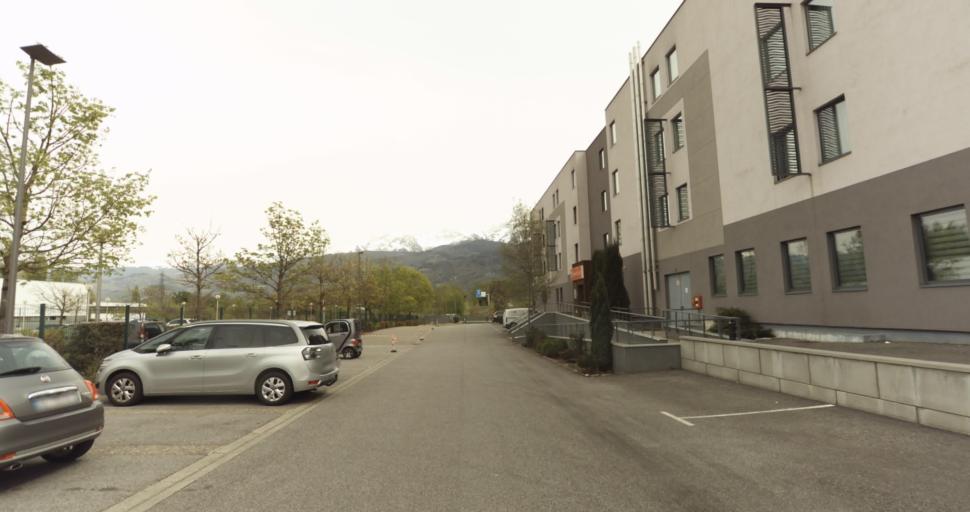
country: FR
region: Rhone-Alpes
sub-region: Departement de l'Isere
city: Montbonnot-Saint-Martin
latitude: 45.2145
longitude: 5.8096
